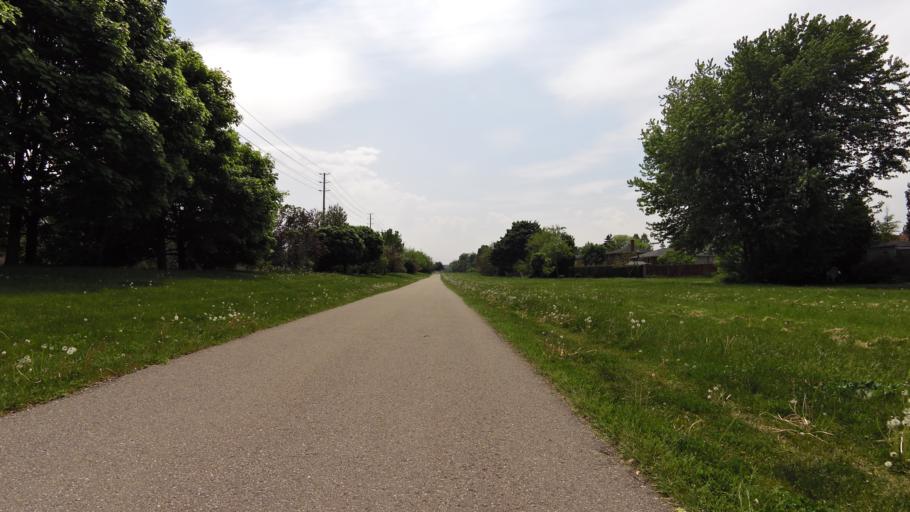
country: CA
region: Ontario
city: Mississauga
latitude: 43.5838
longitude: -79.5969
